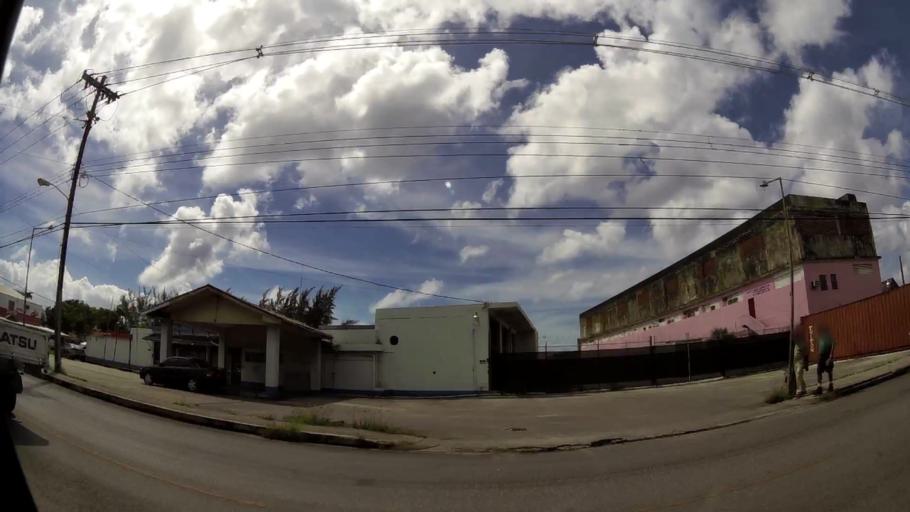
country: BB
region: Saint Michael
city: Bridgetown
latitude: 13.1003
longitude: -59.6228
